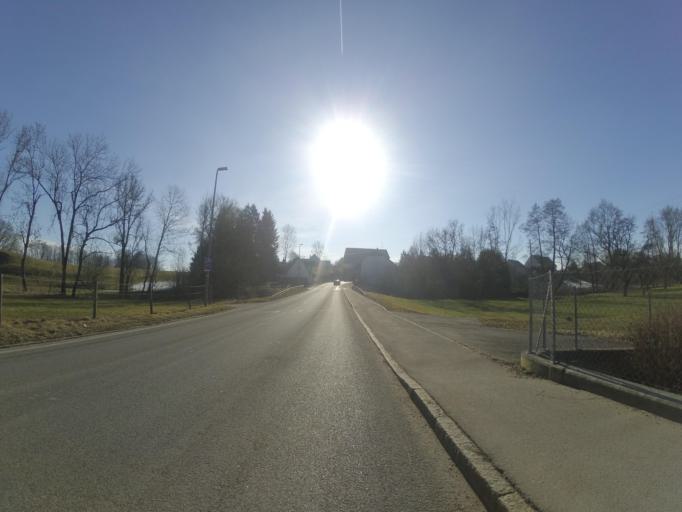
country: DE
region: Baden-Wuerttemberg
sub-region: Tuebingen Region
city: Aulendorf
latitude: 47.9322
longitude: 9.6401
